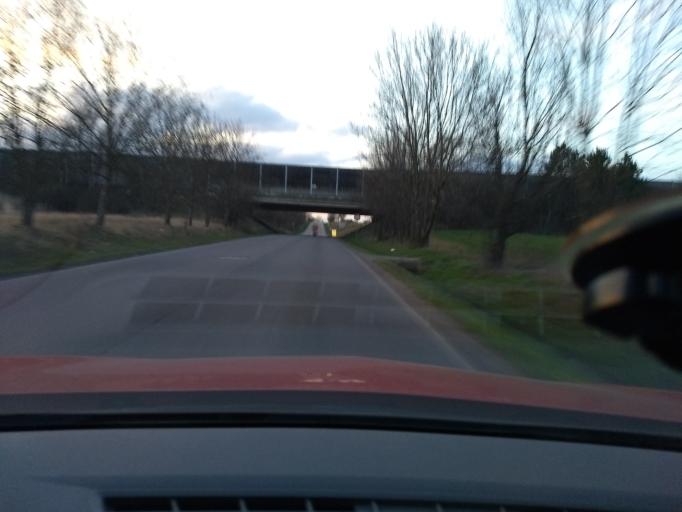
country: CZ
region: Central Bohemia
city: Rudna
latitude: 50.0471
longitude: 14.2570
